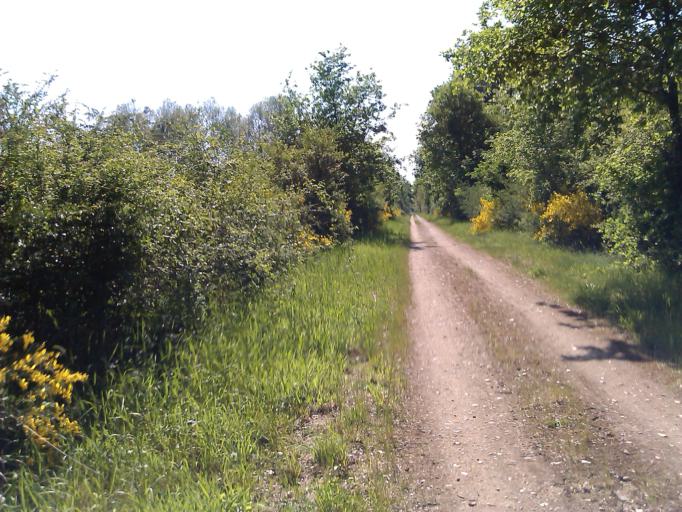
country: FR
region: Centre
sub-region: Departement de l'Indre
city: Belabre
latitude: 46.6268
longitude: 1.2208
